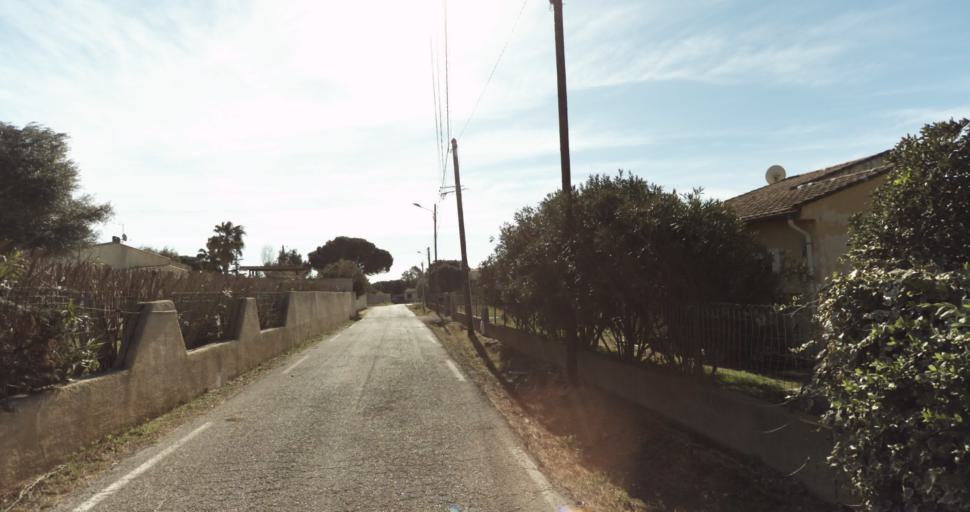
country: FR
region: Languedoc-Roussillon
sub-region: Departement de l'Herault
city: Marseillan
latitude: 43.3364
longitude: 3.5189
